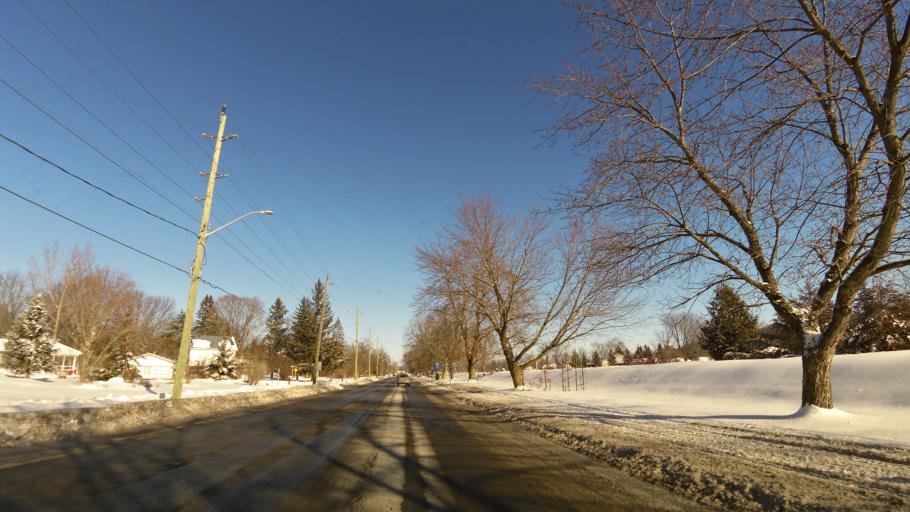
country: CA
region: Ontario
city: Quinte West
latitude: 44.2963
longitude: -77.8061
